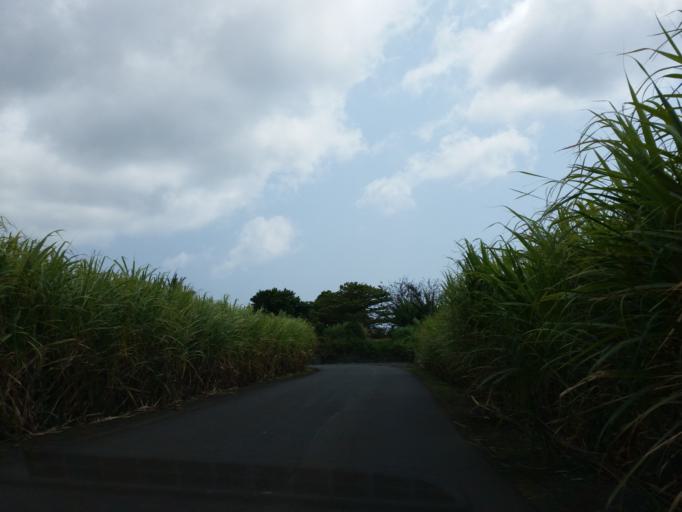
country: RE
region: Reunion
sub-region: Reunion
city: Sainte-Suzanne
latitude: -20.9163
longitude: 55.6162
